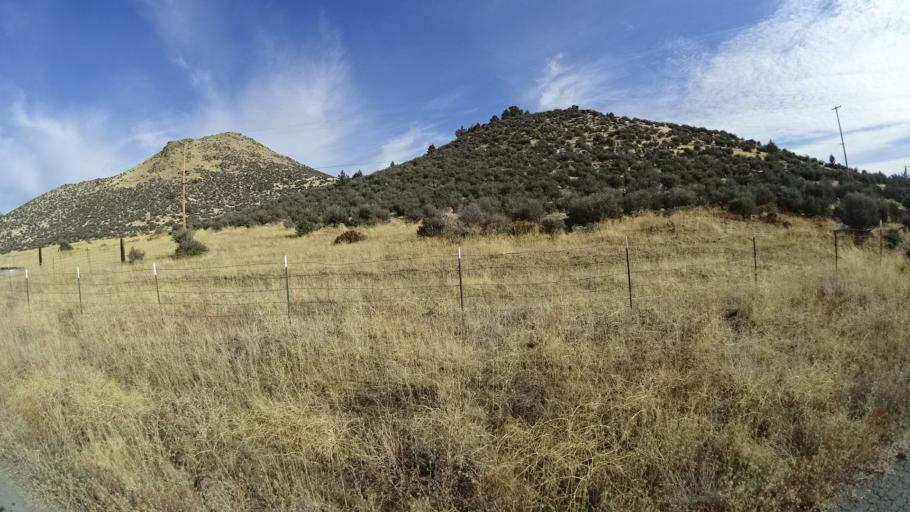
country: US
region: California
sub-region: Siskiyou County
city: Montague
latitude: 41.7080
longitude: -122.5167
